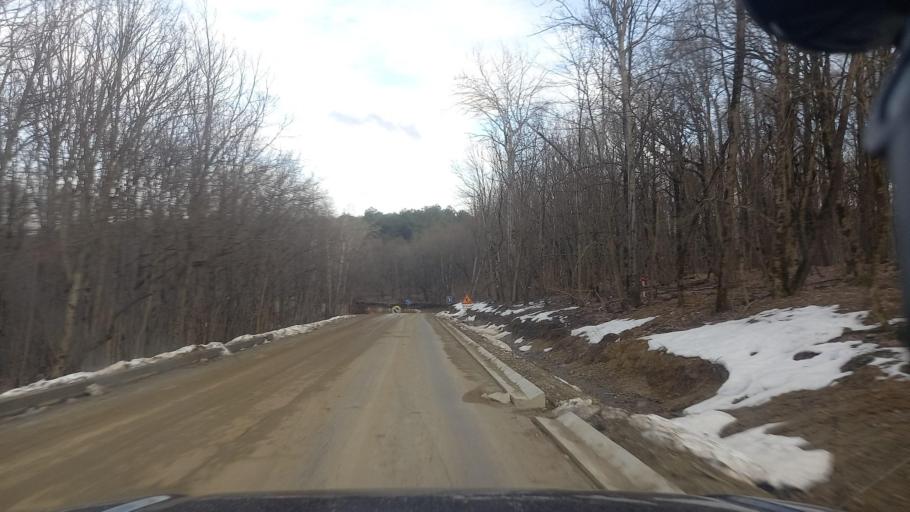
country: RU
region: Krasnodarskiy
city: Goryachiy Klyuch
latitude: 44.6976
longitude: 38.9885
